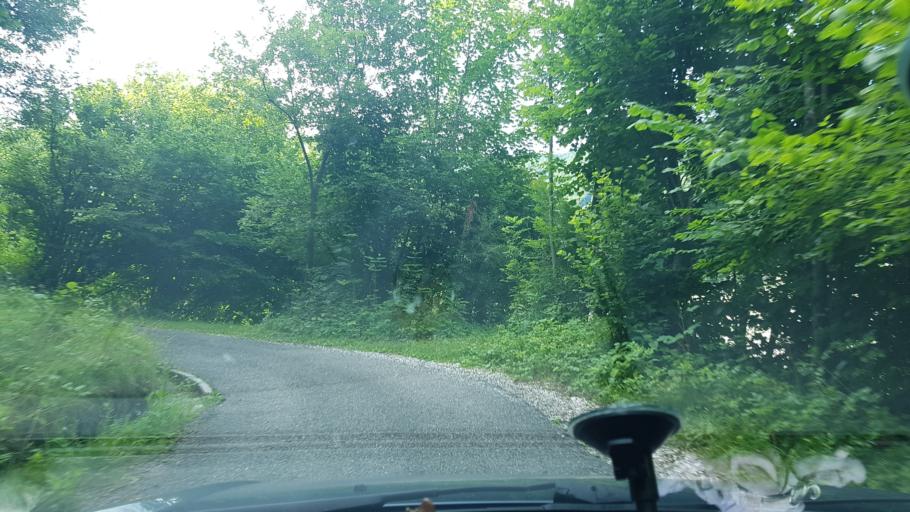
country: IT
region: Friuli Venezia Giulia
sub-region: Provincia di Udine
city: Prato
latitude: 46.3474
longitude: 13.3959
